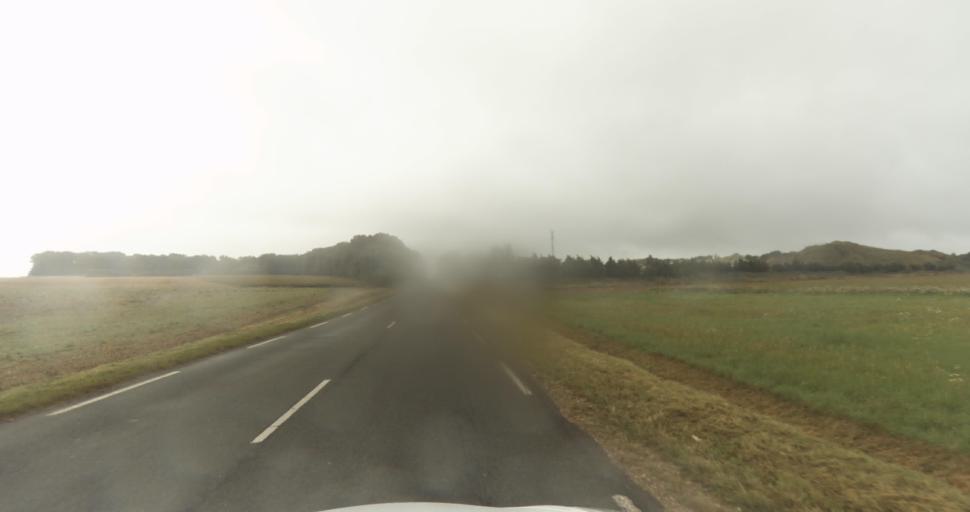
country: FR
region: Haute-Normandie
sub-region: Departement de l'Eure
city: Normanville
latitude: 49.0962
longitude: 1.1749
